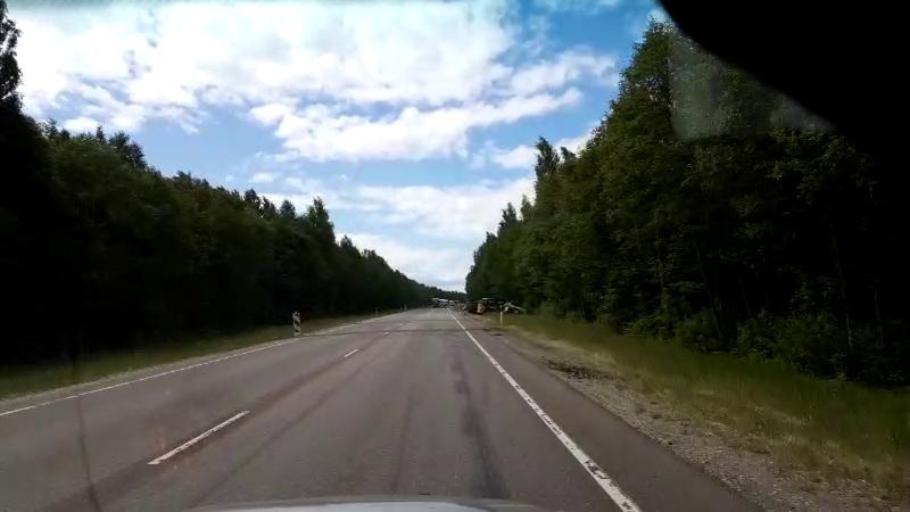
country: LV
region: Salacgrivas
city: Ainazi
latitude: 58.0160
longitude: 24.4954
